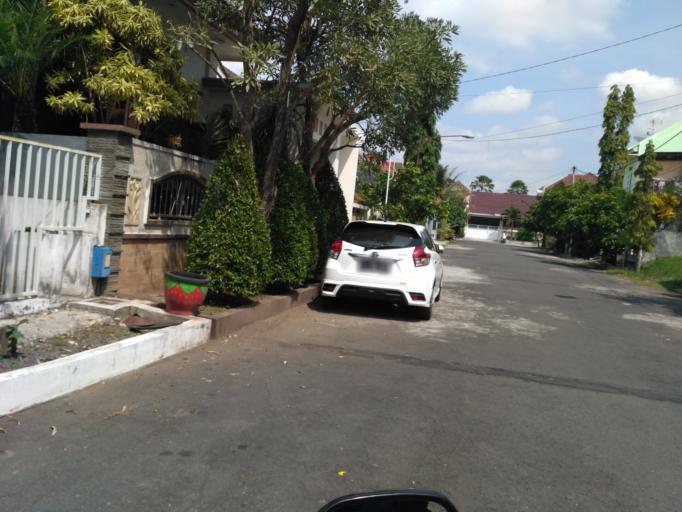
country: ID
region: East Java
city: Malang
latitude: -7.9309
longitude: 112.6126
